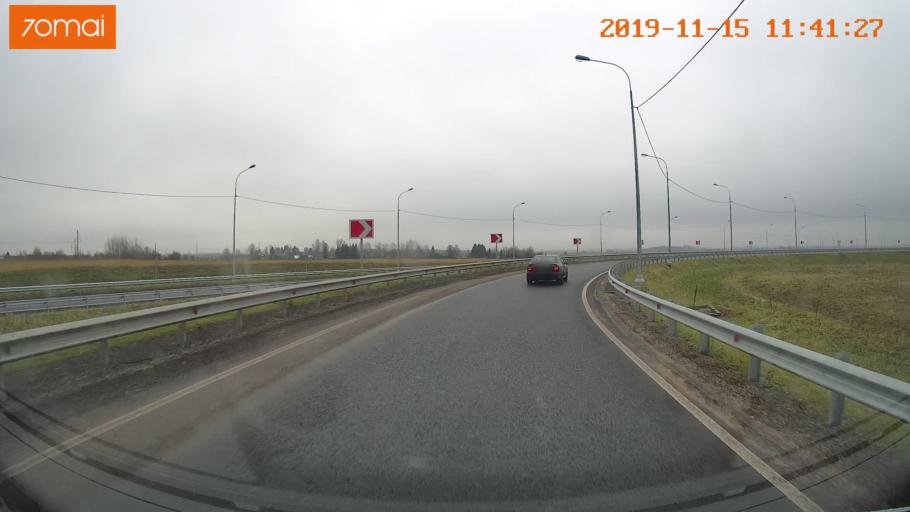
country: RU
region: Vologda
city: Vologda
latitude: 59.2123
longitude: 39.7707
